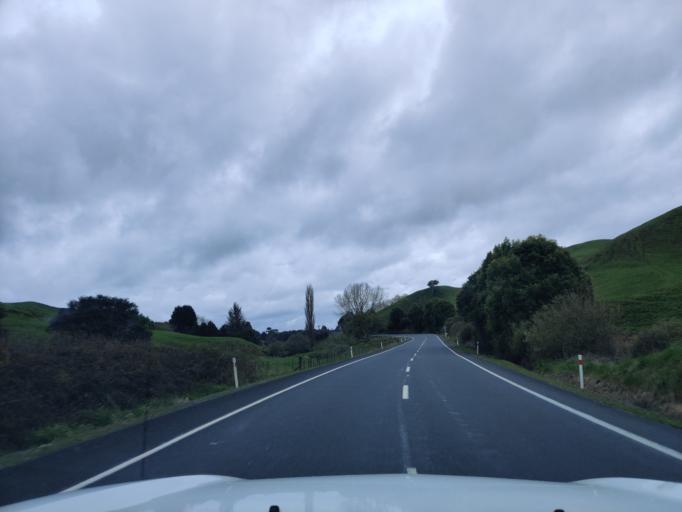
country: NZ
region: Waikato
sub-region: Otorohanga District
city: Otorohanga
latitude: -38.5386
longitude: 175.1785
